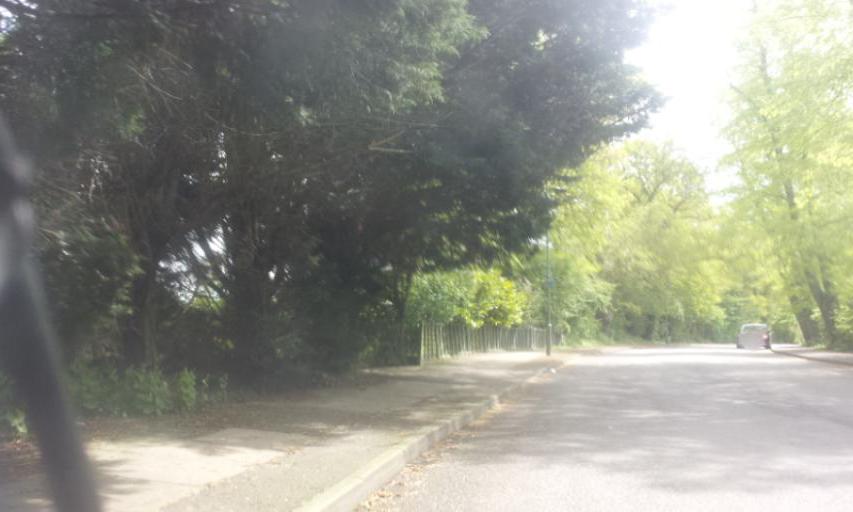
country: GB
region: England
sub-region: Greater London
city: Chislehurst
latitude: 51.3979
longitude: 0.0586
